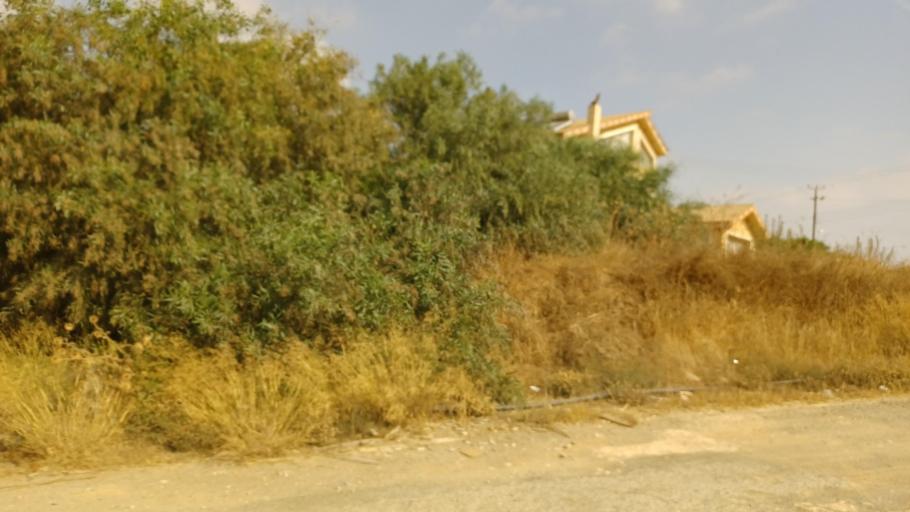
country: CY
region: Ammochostos
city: Paralimni
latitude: 35.0257
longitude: 34.0088
